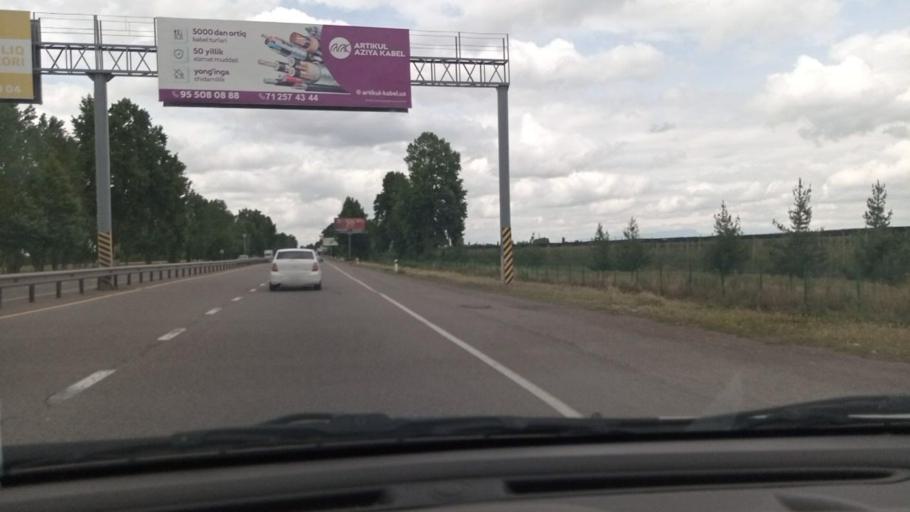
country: UZ
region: Toshkent Shahri
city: Bektemir
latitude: 41.2295
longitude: 69.4024
